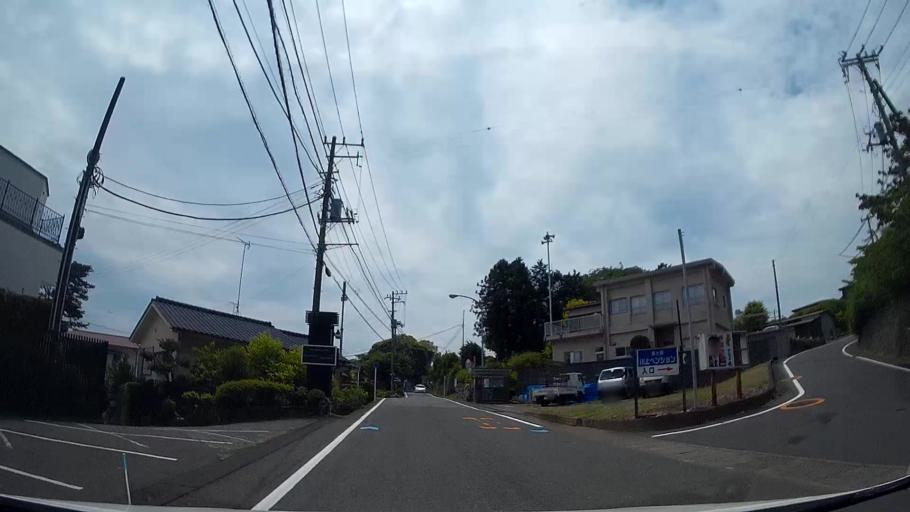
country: JP
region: Shizuoka
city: Ito
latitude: 34.8981
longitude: 139.1310
